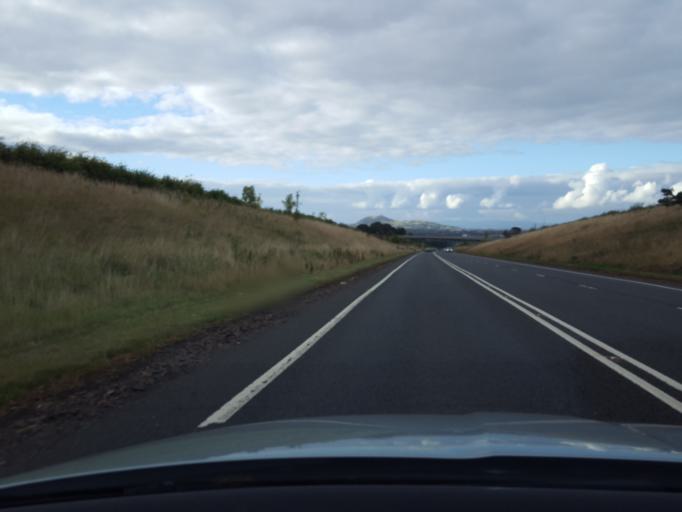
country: GB
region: Scotland
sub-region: Midlothian
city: Dalkeith
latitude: 55.9006
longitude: -3.0222
